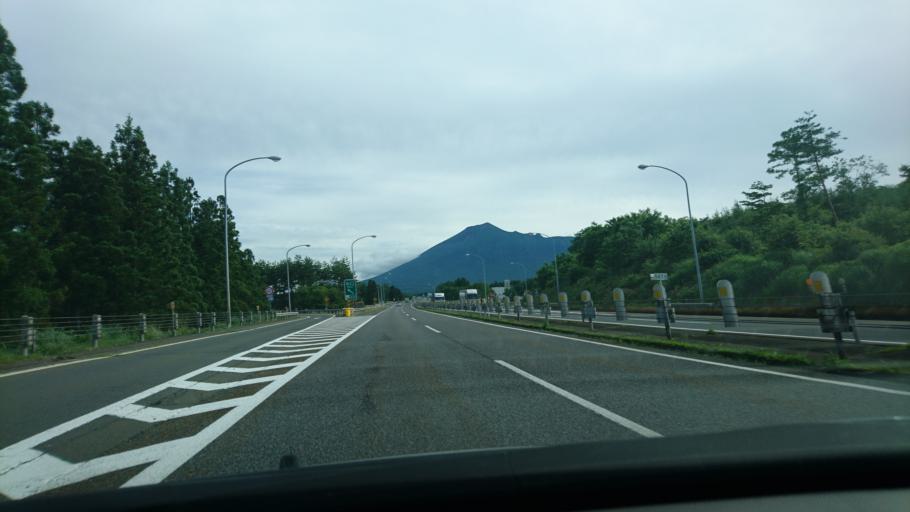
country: JP
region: Iwate
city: Shizukuishi
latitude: 39.9519
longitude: 141.0325
